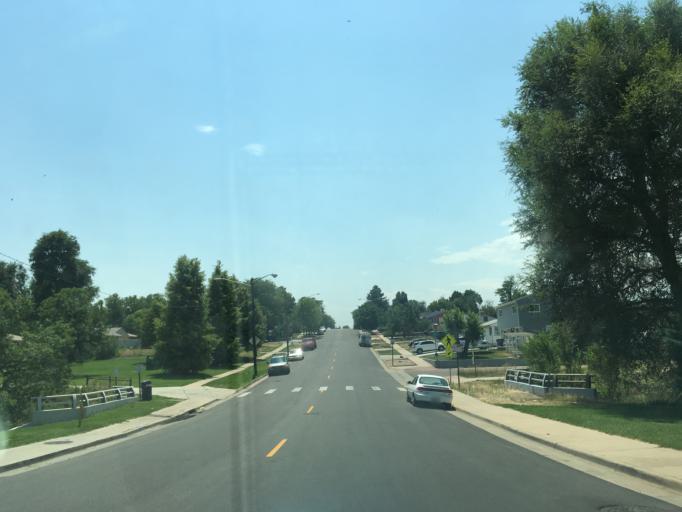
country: US
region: Colorado
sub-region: Arapahoe County
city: Sheridan
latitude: 39.6870
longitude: -105.0299
